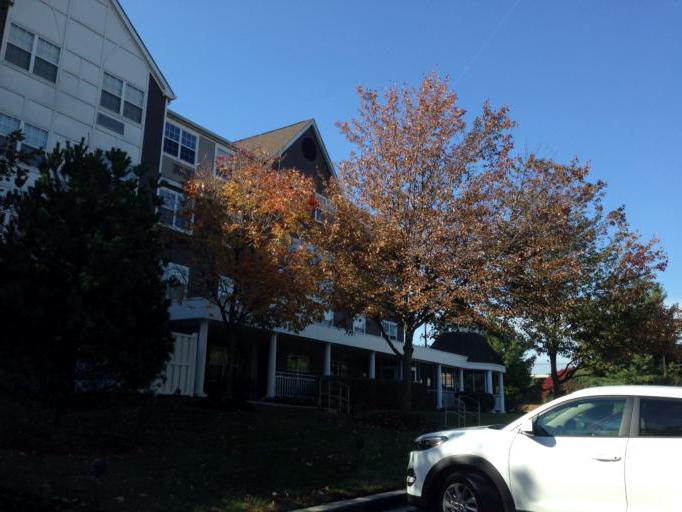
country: US
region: Maryland
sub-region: Howard County
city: Ellicott City
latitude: 39.2786
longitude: -76.8114
